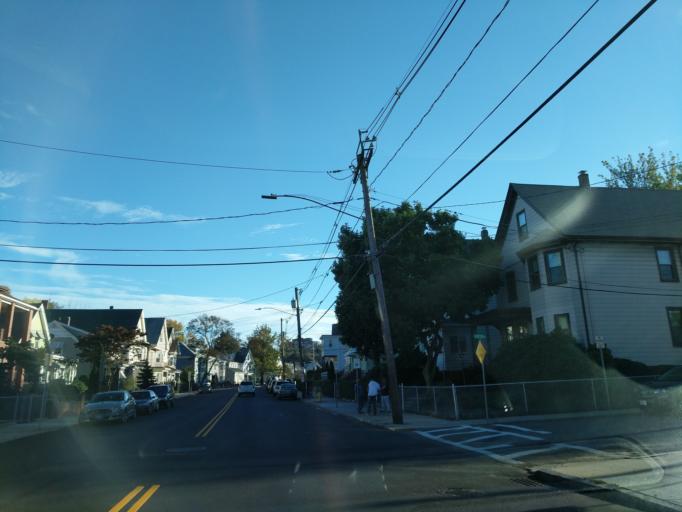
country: US
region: Massachusetts
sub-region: Suffolk County
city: Chelsea
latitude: 42.4077
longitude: -71.0295
